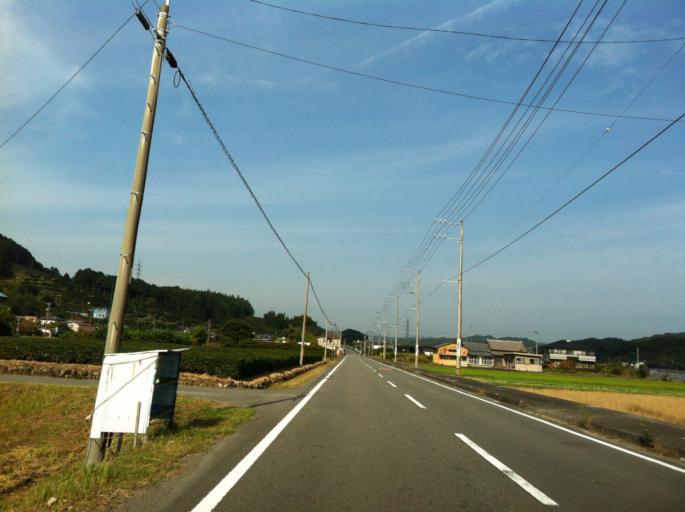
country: JP
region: Shizuoka
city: Shimada
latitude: 34.7653
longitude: 138.1862
